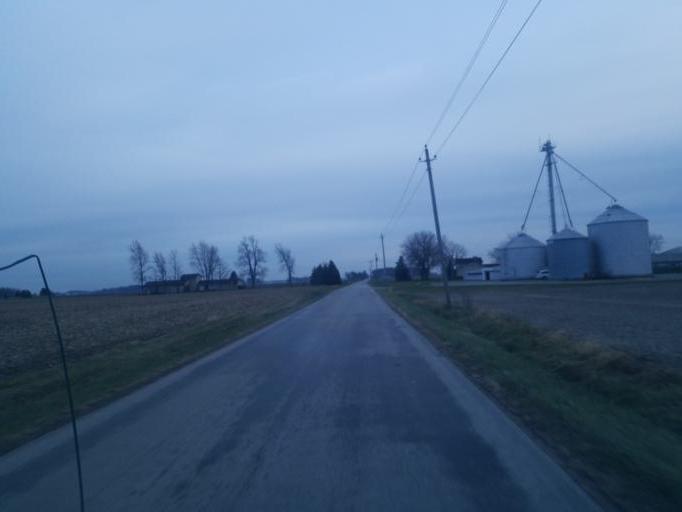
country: US
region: Indiana
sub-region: Adams County
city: Decatur
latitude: 40.7605
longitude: -85.0140
